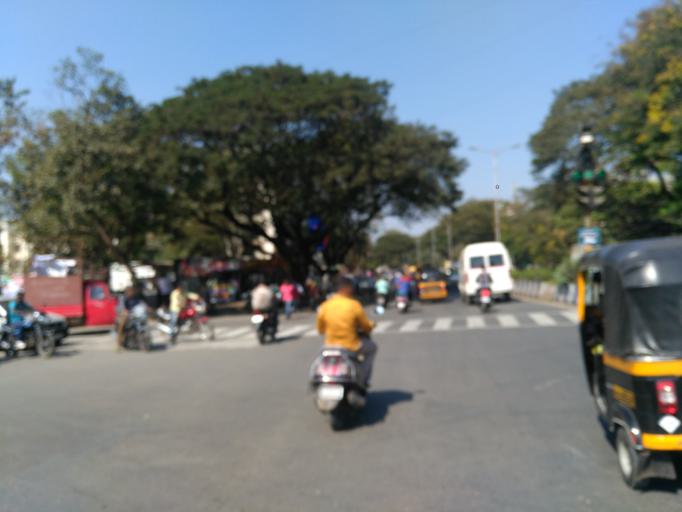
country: IN
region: Maharashtra
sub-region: Pune Division
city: Pune
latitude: 18.4690
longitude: 73.8640
